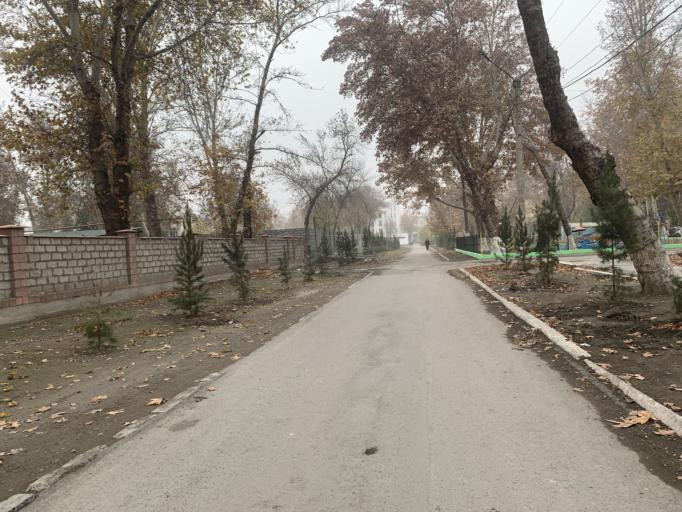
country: UZ
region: Fergana
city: Qo`qon
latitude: 40.5441
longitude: 70.9236
